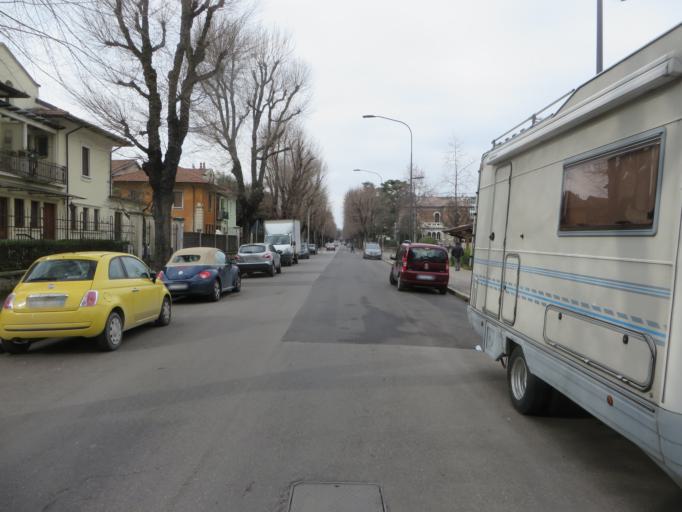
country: IT
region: Lombardy
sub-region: Provincia di Brescia
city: Brescia
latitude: 45.5502
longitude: 10.2186
